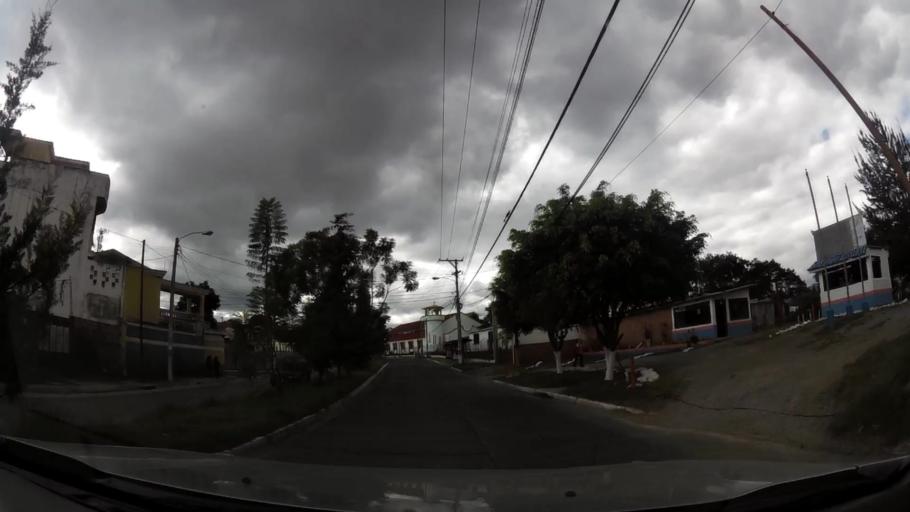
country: GT
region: Guatemala
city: Guatemala City
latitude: 14.6774
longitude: -90.5538
